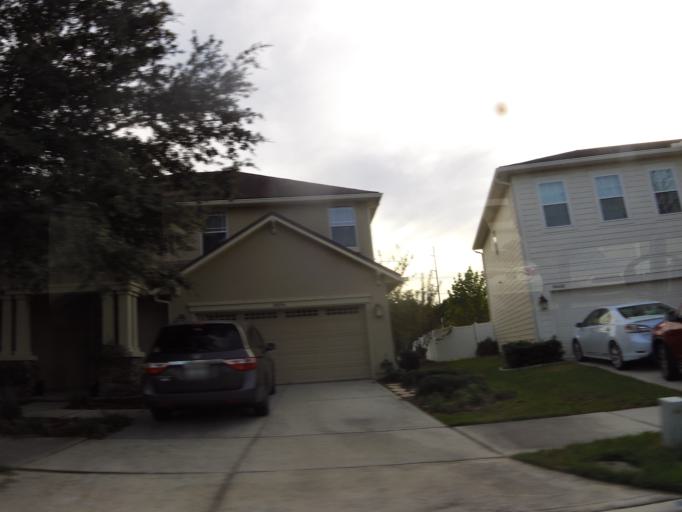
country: US
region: Florida
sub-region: Saint Johns County
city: Fruit Cove
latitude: 30.1485
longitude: -81.5399
